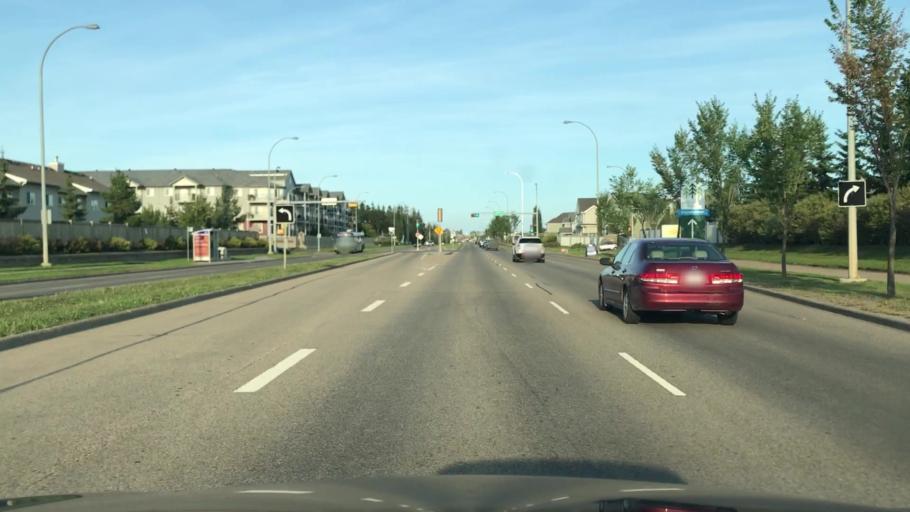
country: CA
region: Alberta
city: Beaumont
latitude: 53.4249
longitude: -113.4571
